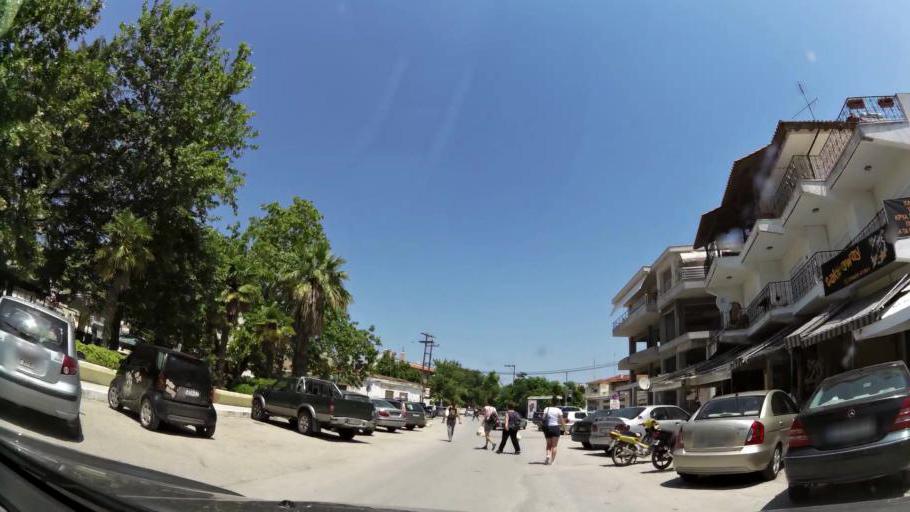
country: GR
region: Central Macedonia
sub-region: Nomos Thessalonikis
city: Epanomi
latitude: 40.4275
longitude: 22.9293
